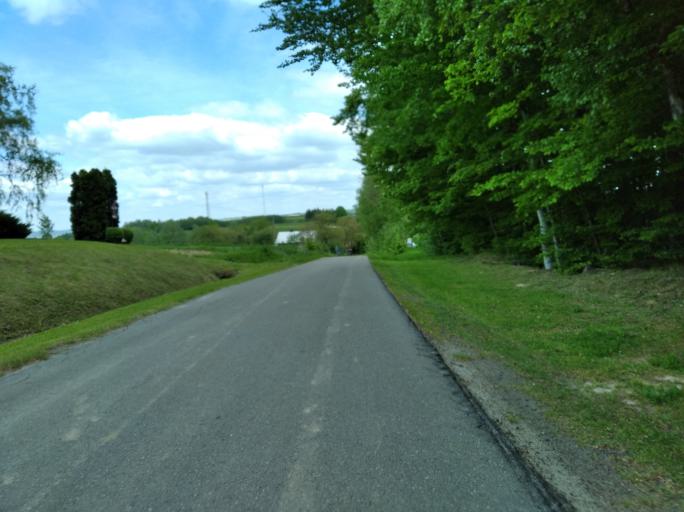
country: PL
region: Subcarpathian Voivodeship
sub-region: Powiat ropczycko-sedziszowski
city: Wielopole Skrzynskie
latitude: 49.9317
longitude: 21.6007
